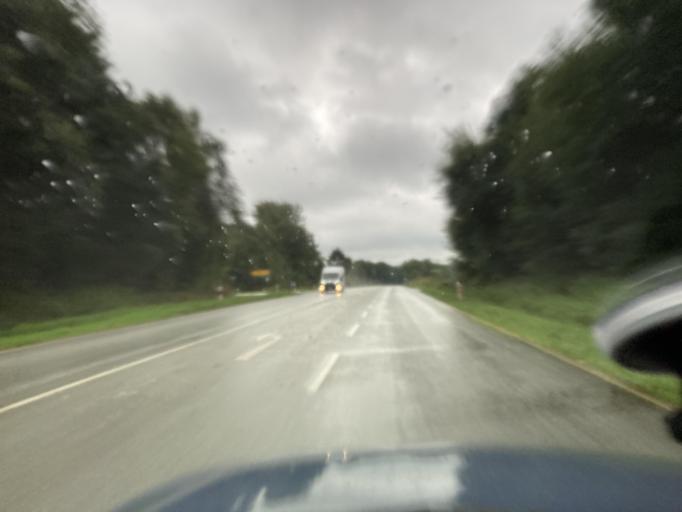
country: DE
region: Schleswig-Holstein
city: Suderdorf
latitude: 54.2194
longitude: 9.3459
